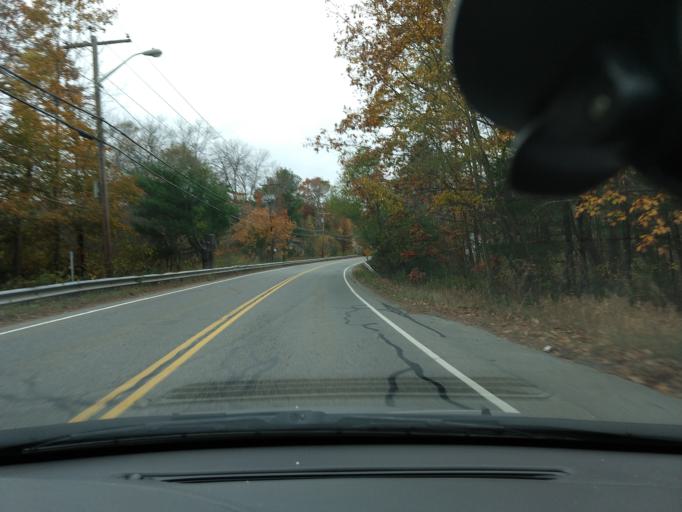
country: US
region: Massachusetts
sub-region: Middlesex County
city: Billerica
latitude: 42.5362
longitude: -71.3015
